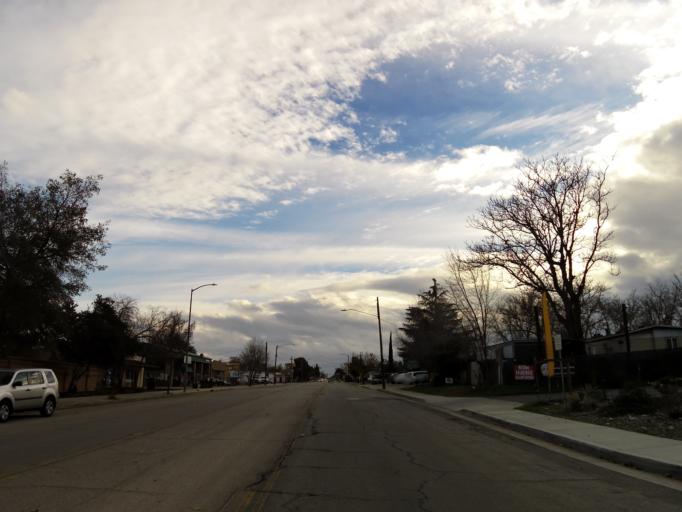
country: US
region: California
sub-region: San Luis Obispo County
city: Paso Robles
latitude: 35.6451
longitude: -120.6930
